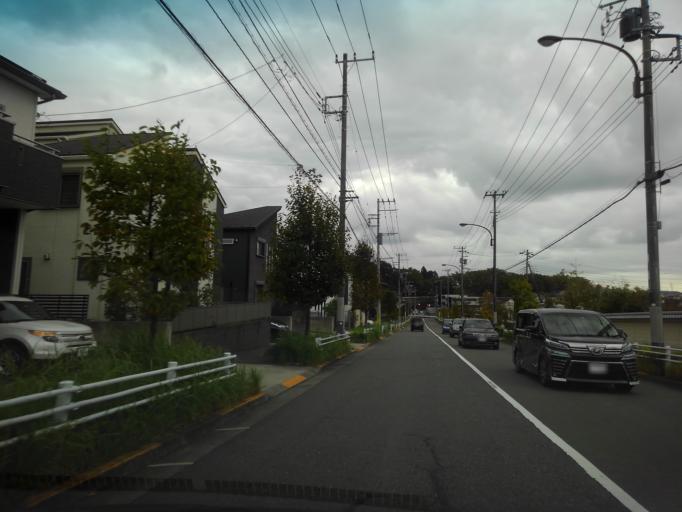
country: JP
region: Tokyo
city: Hino
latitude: 35.5960
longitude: 139.3870
